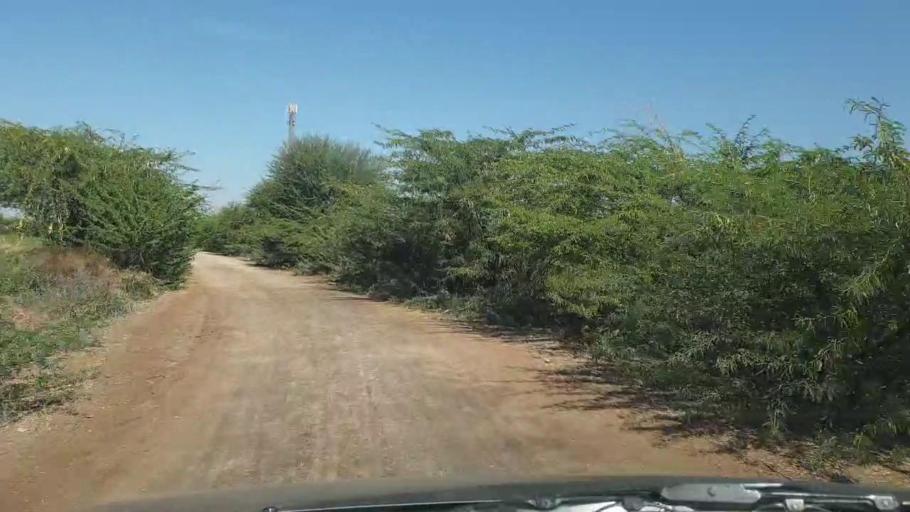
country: PK
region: Sindh
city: Umarkot
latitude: 25.4052
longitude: 69.6362
